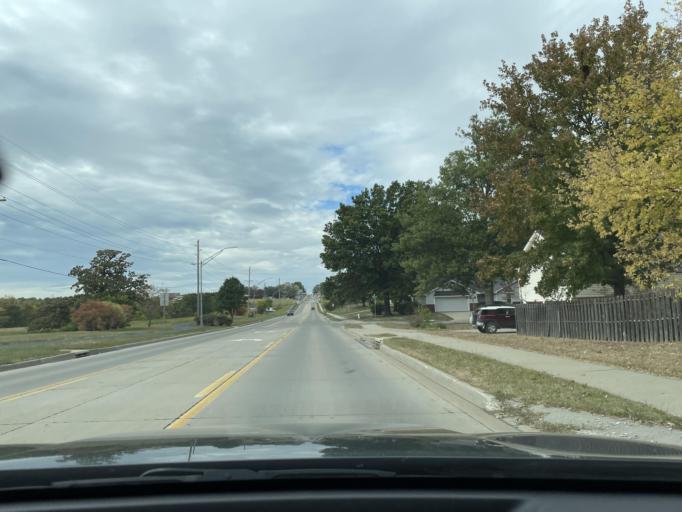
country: US
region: Missouri
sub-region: Buchanan County
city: Saint Joseph
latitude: 39.7698
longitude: -94.7872
